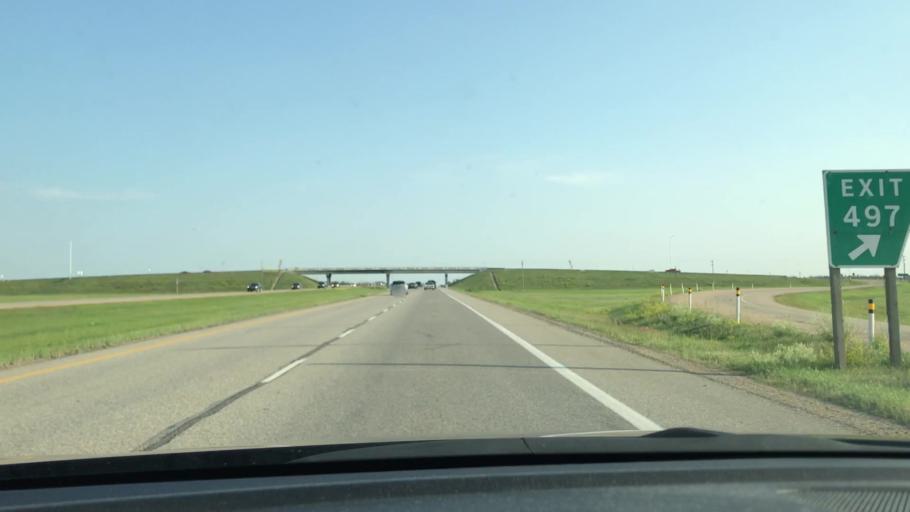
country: CA
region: Alberta
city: Millet
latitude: 53.0937
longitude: -113.5983
